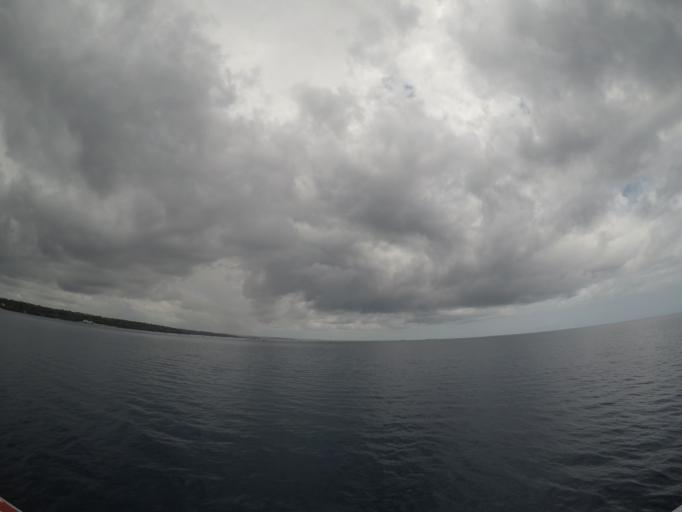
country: TZ
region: Zanzibar North
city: Mkokotoni
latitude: -5.9843
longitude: 39.1736
